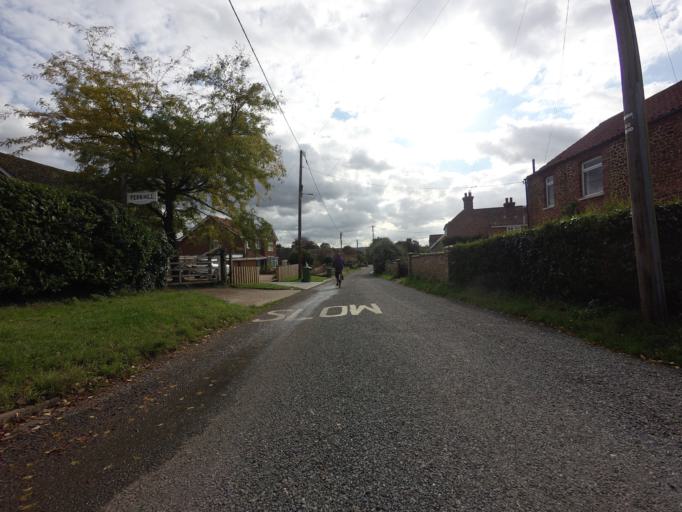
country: GB
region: England
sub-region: Norfolk
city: Dersingham
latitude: 52.8479
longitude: 0.5088
